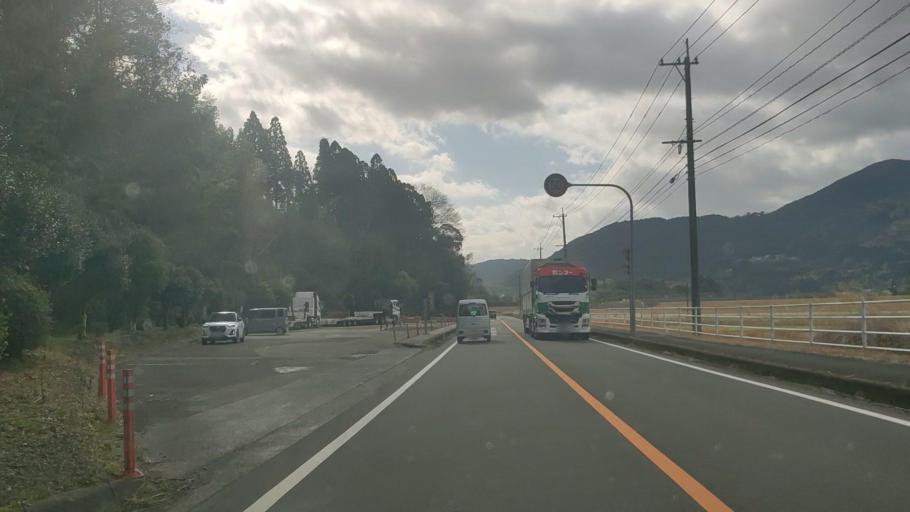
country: JP
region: Kagoshima
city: Okuchi-shinohara
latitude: 32.0293
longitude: 130.7431
